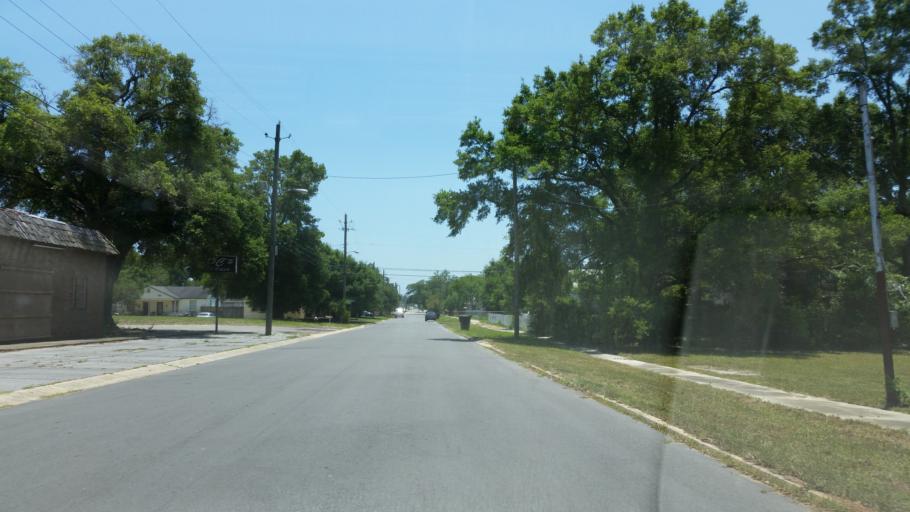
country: US
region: Florida
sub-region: Escambia County
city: Pensacola
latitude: 30.4107
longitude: -87.2351
